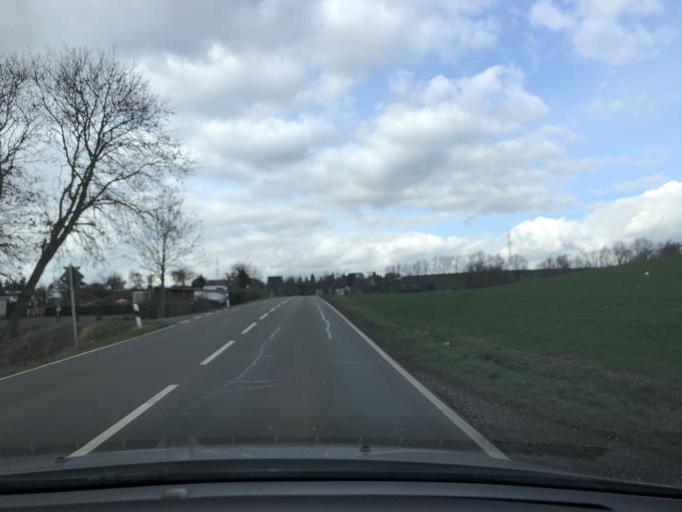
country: DE
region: Saxony
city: Dobeln
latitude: 51.1400
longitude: 13.0957
